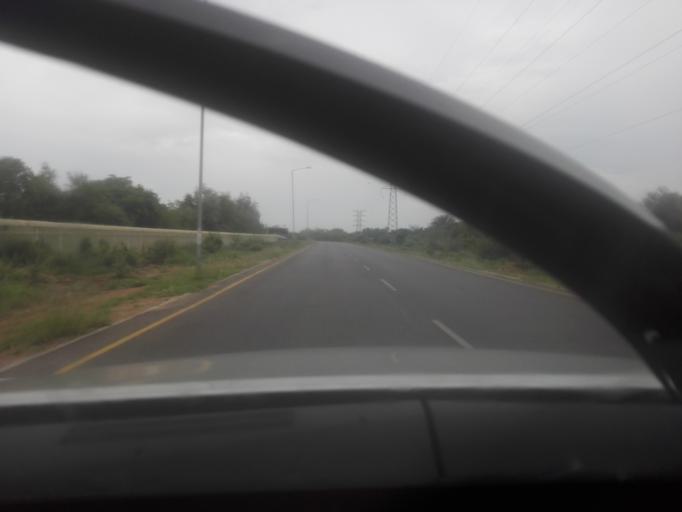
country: BW
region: South East
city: Gaborone
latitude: -24.6380
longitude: 25.8985
